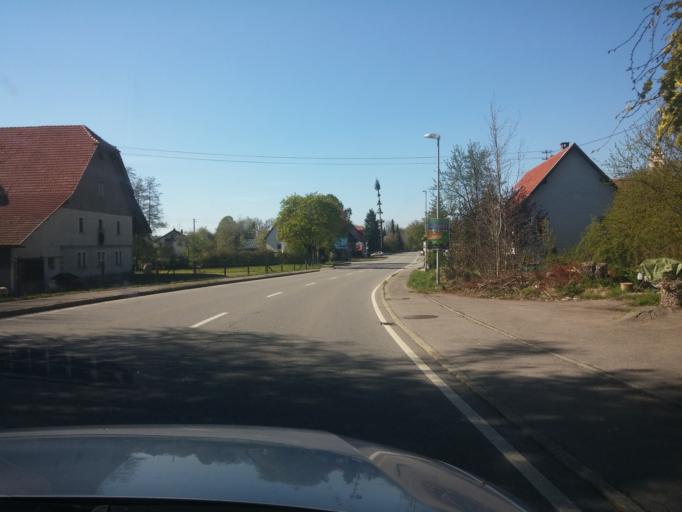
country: DE
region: Baden-Wuerttemberg
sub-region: Tuebingen Region
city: Bad Wurzach
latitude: 47.9476
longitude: 9.8507
